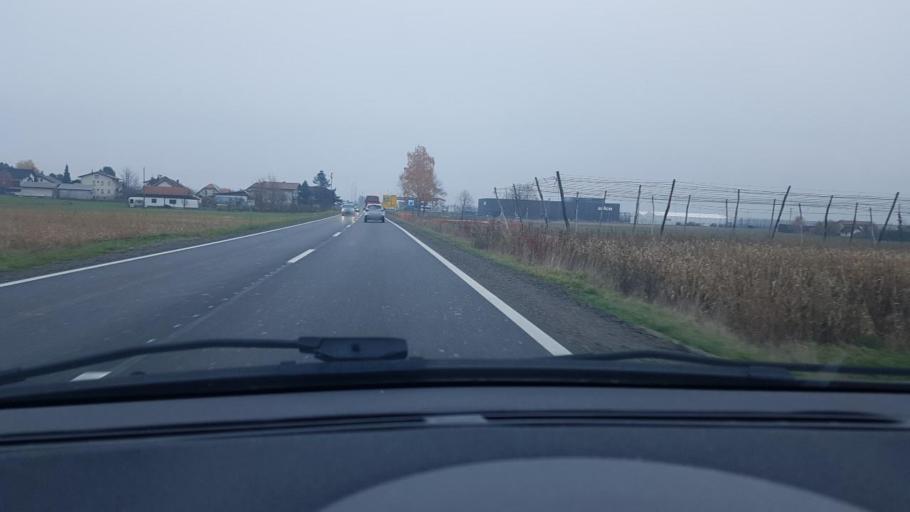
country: SI
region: Prebold
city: Prebold
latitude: 46.2494
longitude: 15.0710
